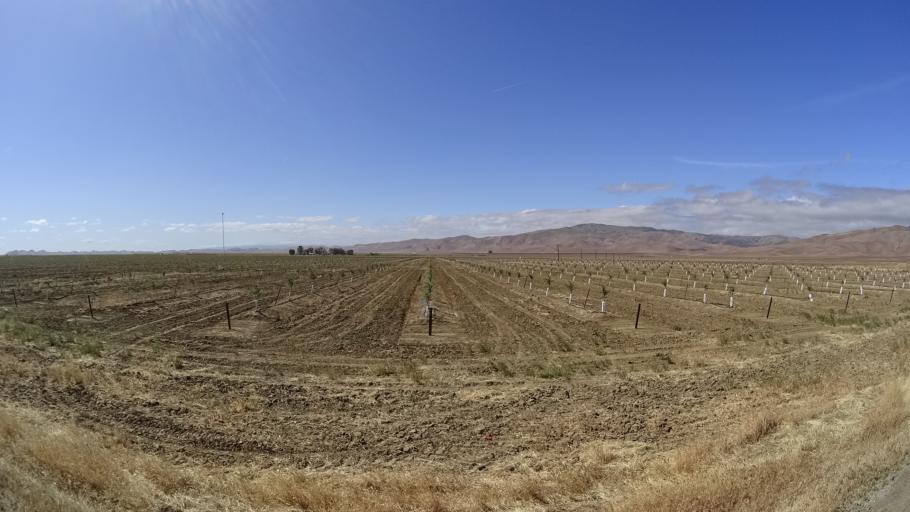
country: US
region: California
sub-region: Kings County
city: Avenal
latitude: 35.8178
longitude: -120.0932
